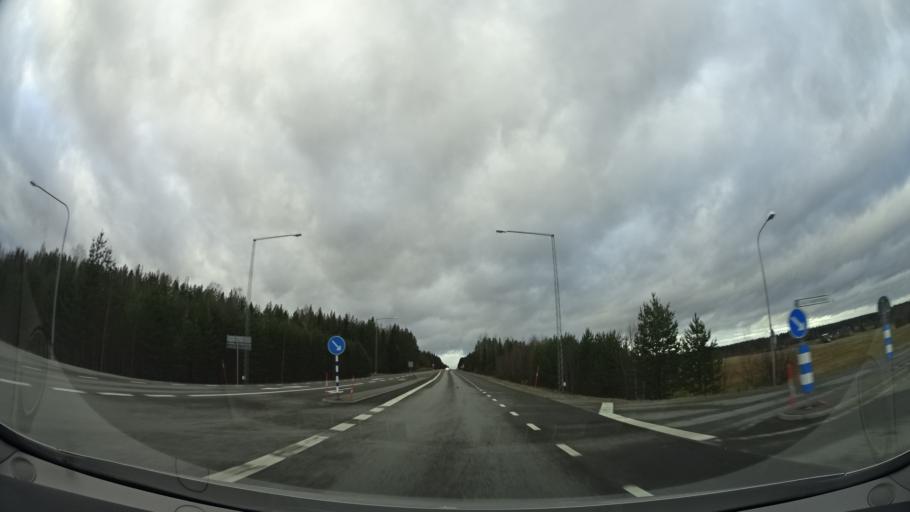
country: SE
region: Vaesterbotten
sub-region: Skelleftea Kommun
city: Viken
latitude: 64.7630
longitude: 20.8807
